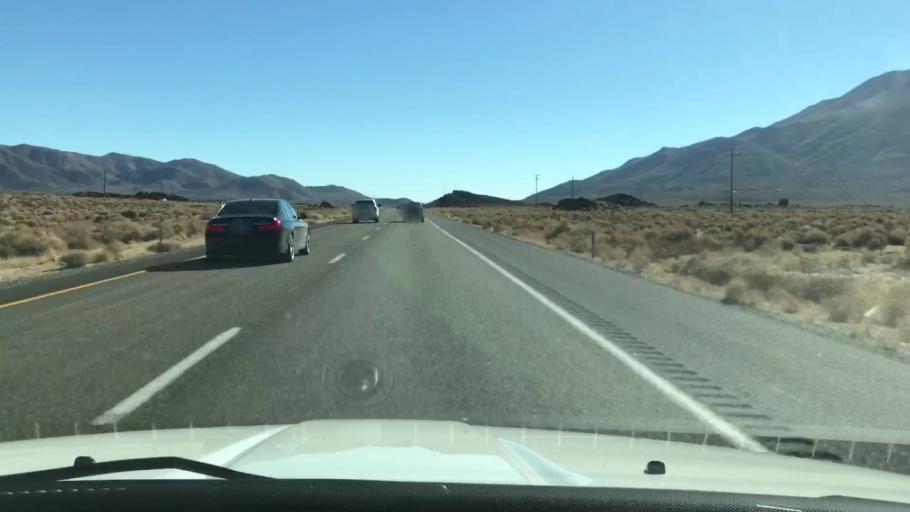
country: US
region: California
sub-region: Kern County
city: Inyokern
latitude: 35.9833
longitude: -117.9266
